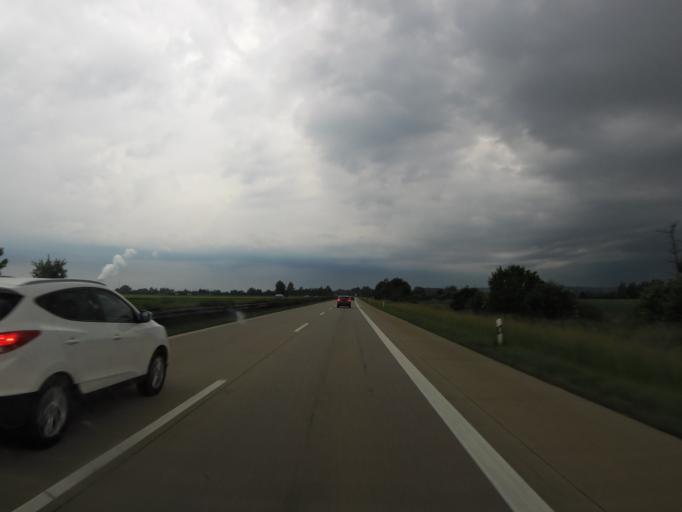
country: DE
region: Bavaria
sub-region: Lower Bavaria
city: Niederviehbach
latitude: 48.6356
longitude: 12.3640
